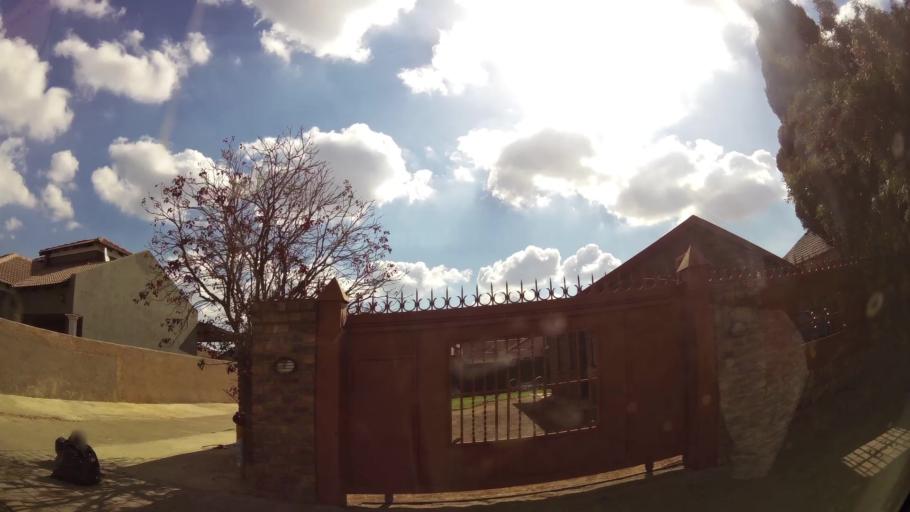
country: ZA
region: Gauteng
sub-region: City of Tshwane Metropolitan Municipality
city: Cullinan
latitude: -25.7086
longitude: 28.4169
